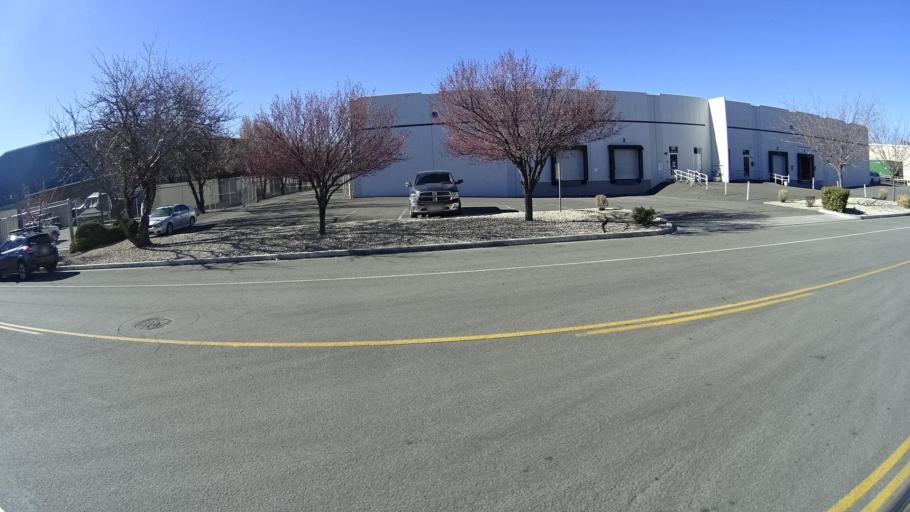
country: US
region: Nevada
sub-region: Washoe County
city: Sparks
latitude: 39.5078
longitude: -119.7576
